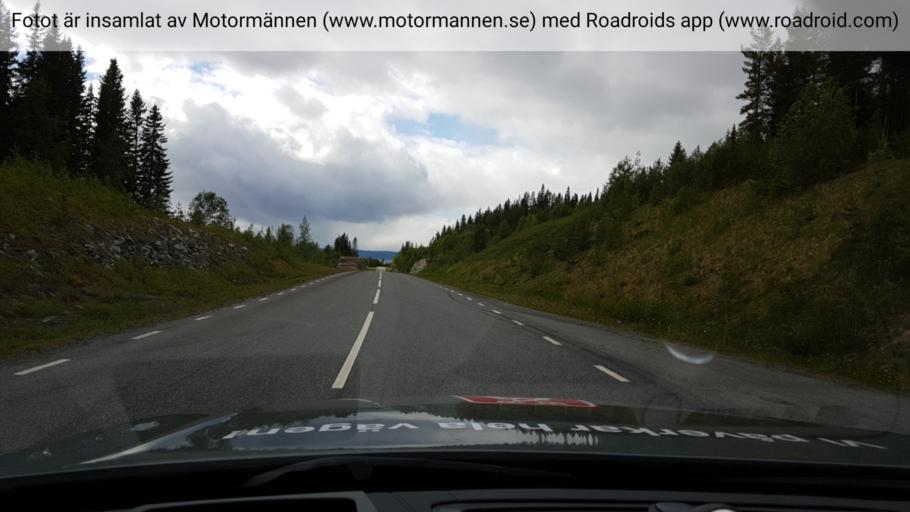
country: SE
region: Jaemtland
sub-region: Are Kommun
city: Are
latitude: 63.6373
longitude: 13.1009
